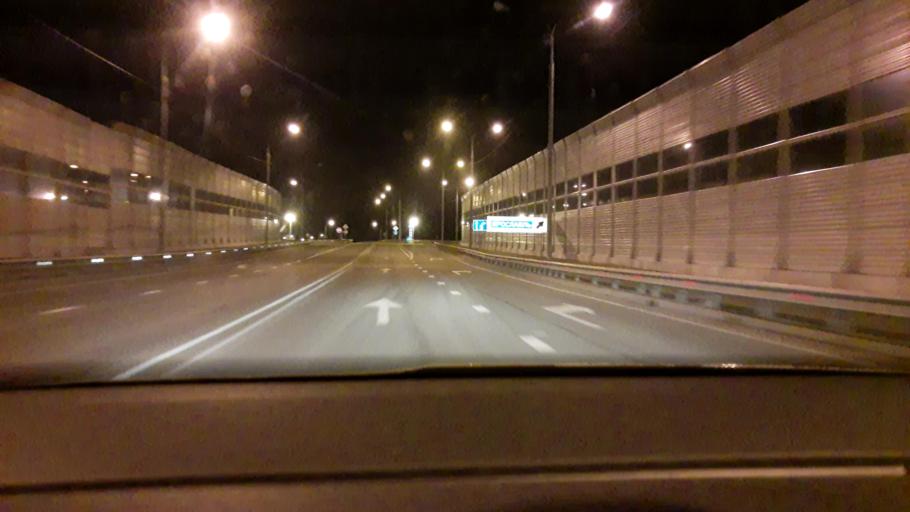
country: RU
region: Moskovskaya
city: Bolshevo
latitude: 55.9508
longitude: 37.8293
